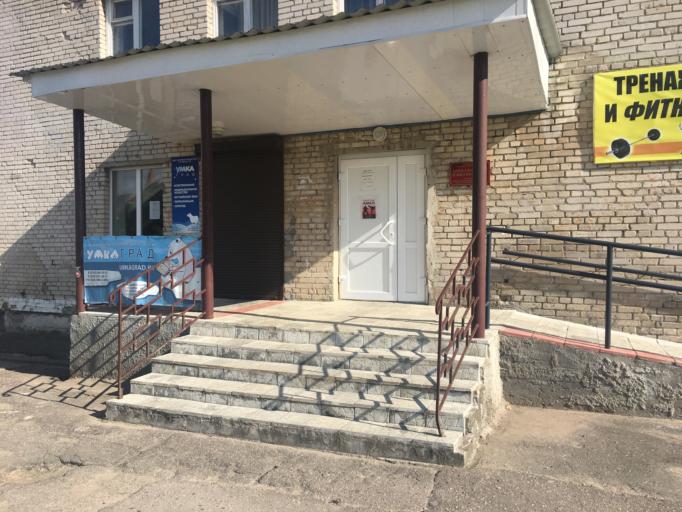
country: BY
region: Grodnenskaya
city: Hrodna
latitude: 53.7088
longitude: 23.8118
